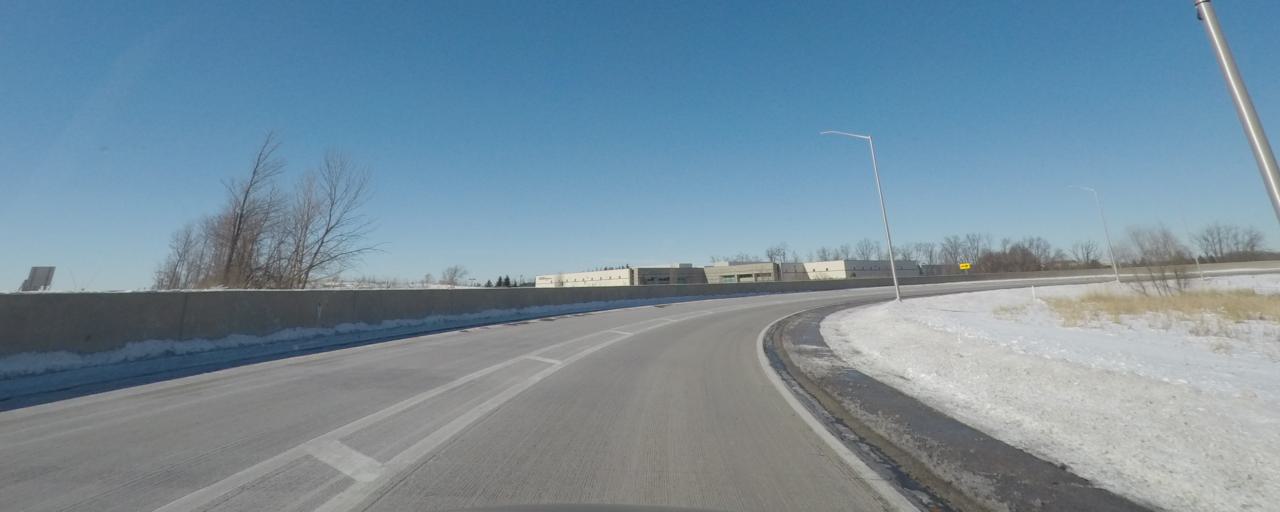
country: US
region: Wisconsin
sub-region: Waukesha County
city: New Berlin
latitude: 42.9495
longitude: -88.1111
